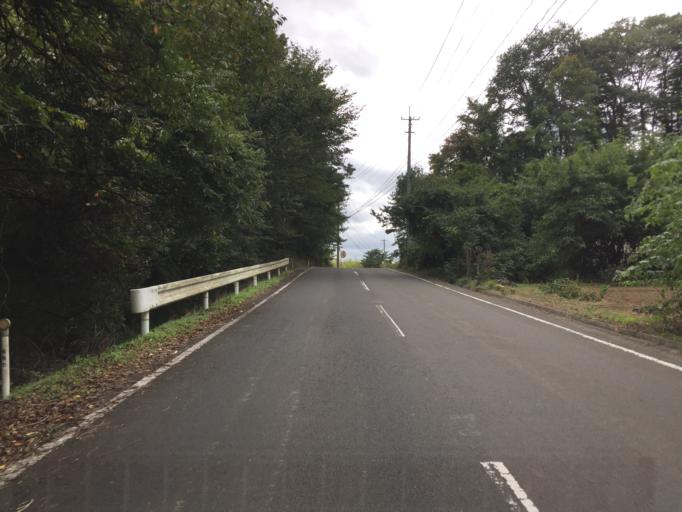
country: JP
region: Fukushima
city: Fukushima-shi
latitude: 37.6867
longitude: 140.4811
